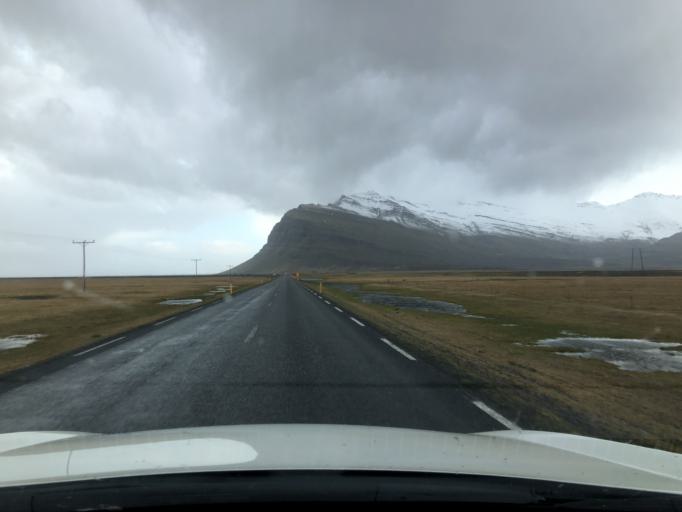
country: IS
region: East
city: Hoefn
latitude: 64.1637
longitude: -15.9225
